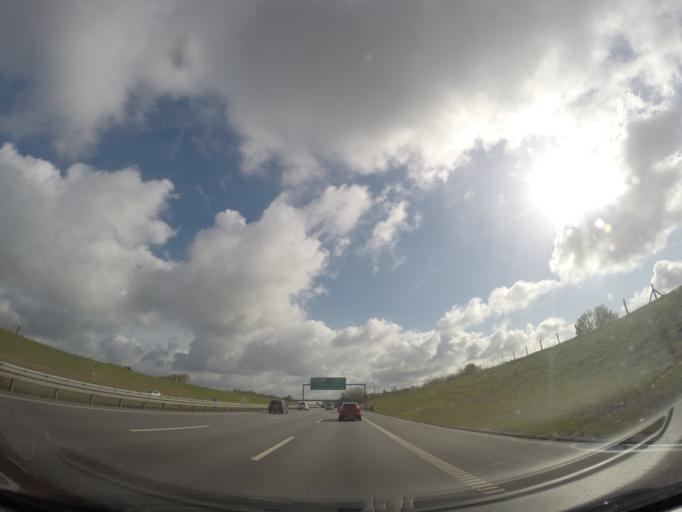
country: DK
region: Capital Region
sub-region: Albertslund Kommune
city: Albertslund
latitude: 55.6878
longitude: 12.3433
